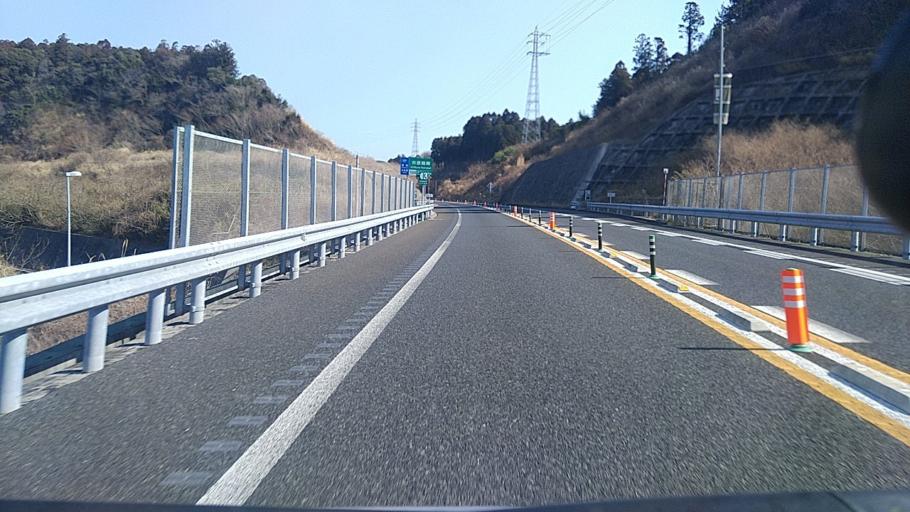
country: JP
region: Chiba
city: Mobara
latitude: 35.3557
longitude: 140.1731
